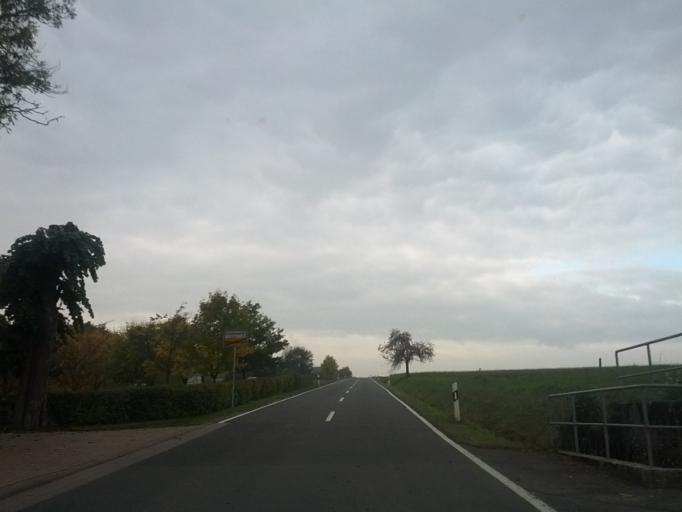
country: DE
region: Hesse
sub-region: Regierungsbezirk Kassel
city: Herleshausen
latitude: 51.0367
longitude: 10.1764
